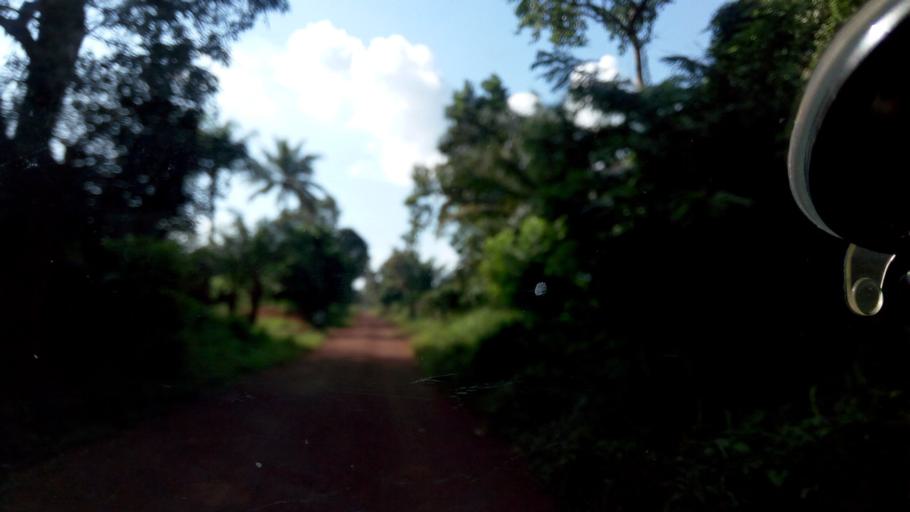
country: CD
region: Equateur
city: Libenge
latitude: 3.8159
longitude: 18.6996
